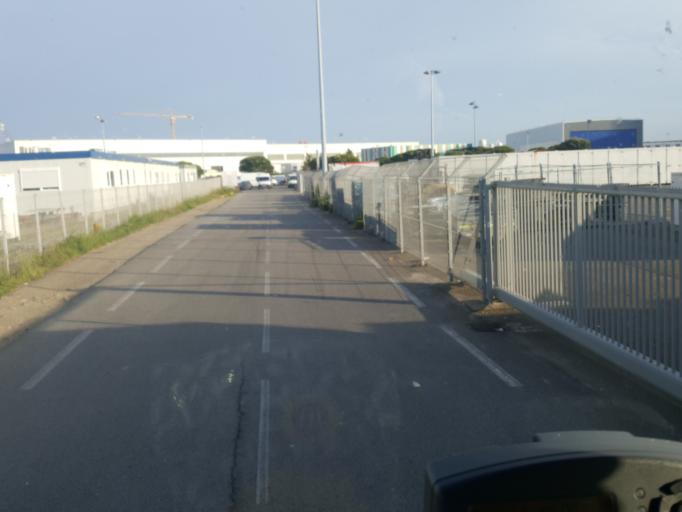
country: FR
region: Pays de la Loire
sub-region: Departement de la Loire-Atlantique
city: Saint-Nazaire
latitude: 47.2798
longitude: -2.1894
